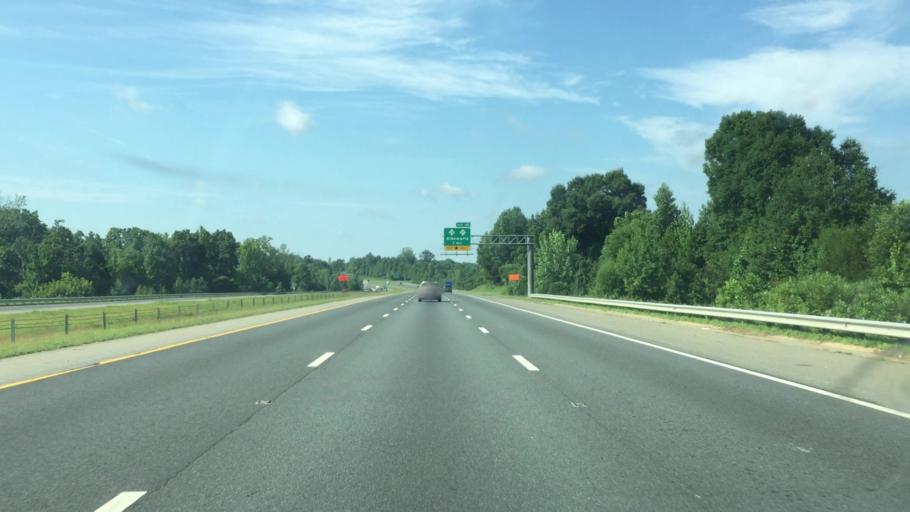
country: US
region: North Carolina
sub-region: Mecklenburg County
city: Mint Hill
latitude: 35.2391
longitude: -80.6515
